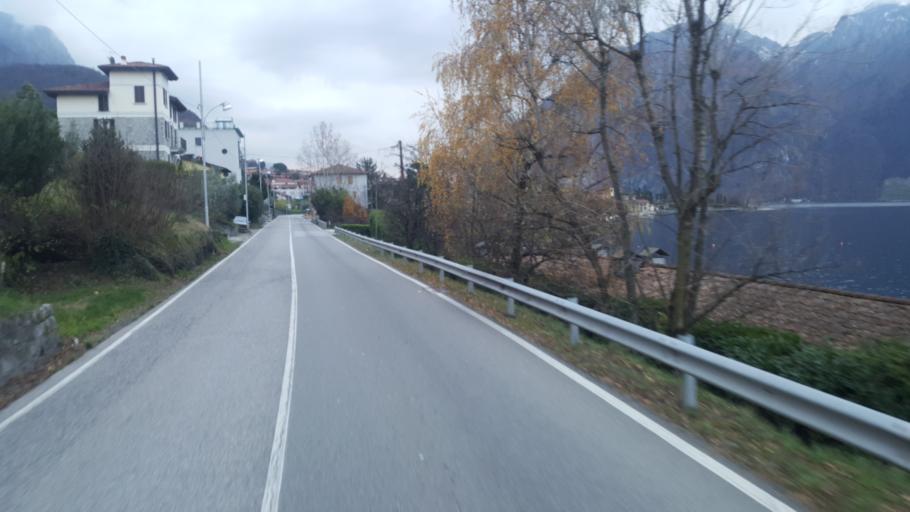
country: IT
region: Lombardy
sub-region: Provincia di Lecco
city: Abbadia Lariana
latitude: 45.9052
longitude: 9.3293
